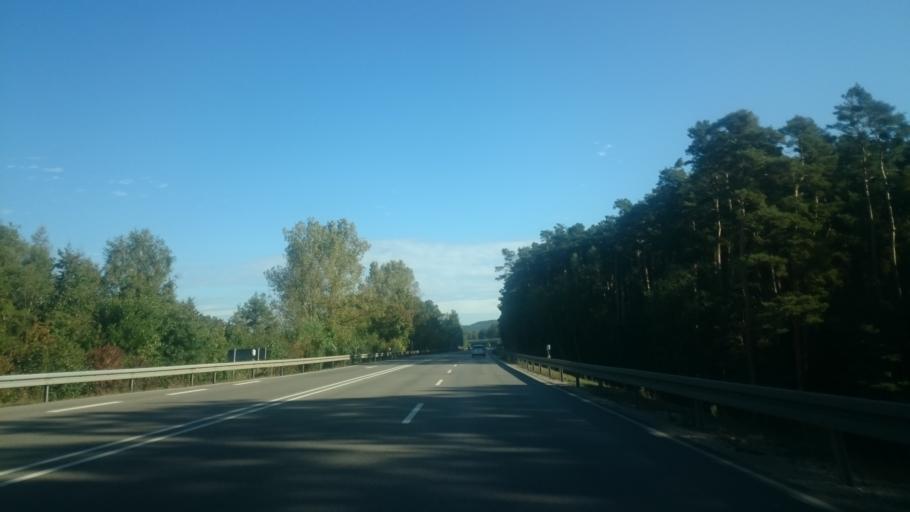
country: DE
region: Bavaria
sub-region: Regierungsbezirk Mittelfranken
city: Pleinfeld
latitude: 49.1118
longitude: 11.0027
